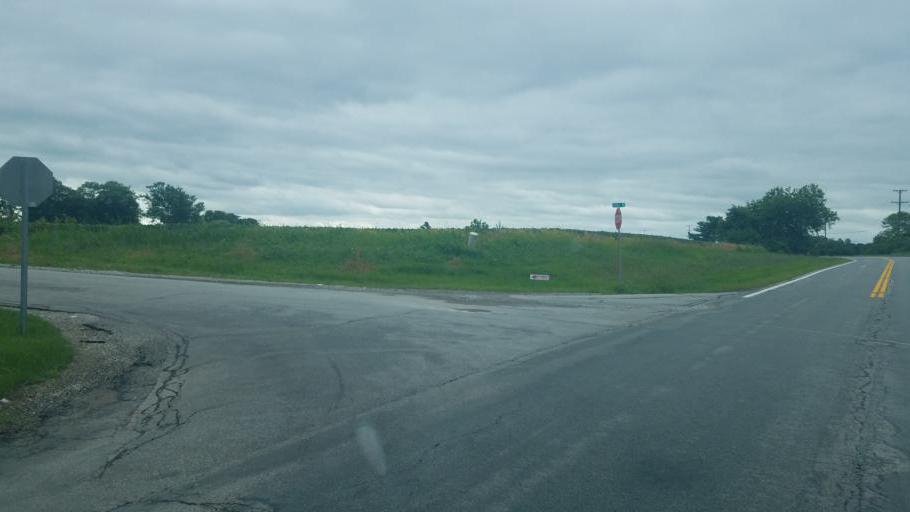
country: US
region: Ohio
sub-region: Franklin County
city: Grove City
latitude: 39.8398
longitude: -83.0303
